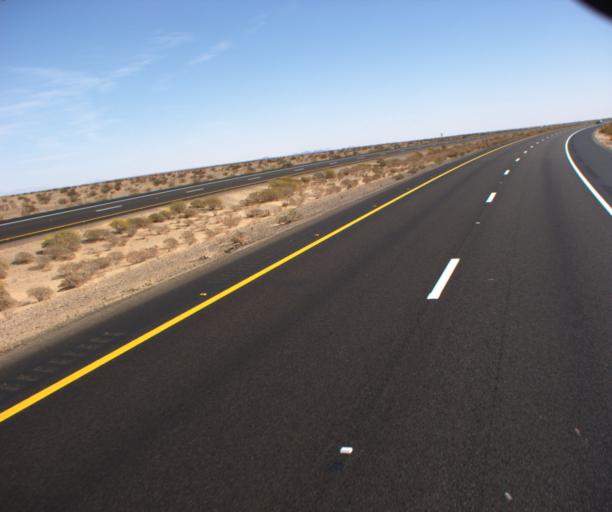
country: US
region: Arizona
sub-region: Yuma County
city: Somerton
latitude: 32.5087
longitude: -114.5589
